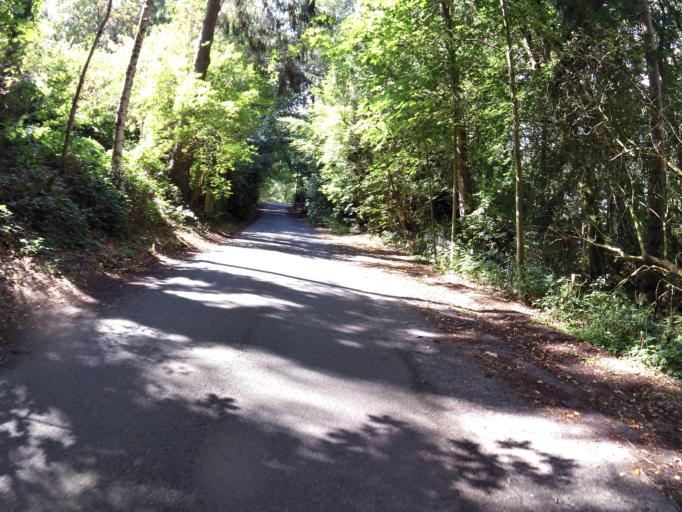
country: DE
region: Lower Saxony
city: Seedorf
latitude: 53.3327
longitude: 9.1987
